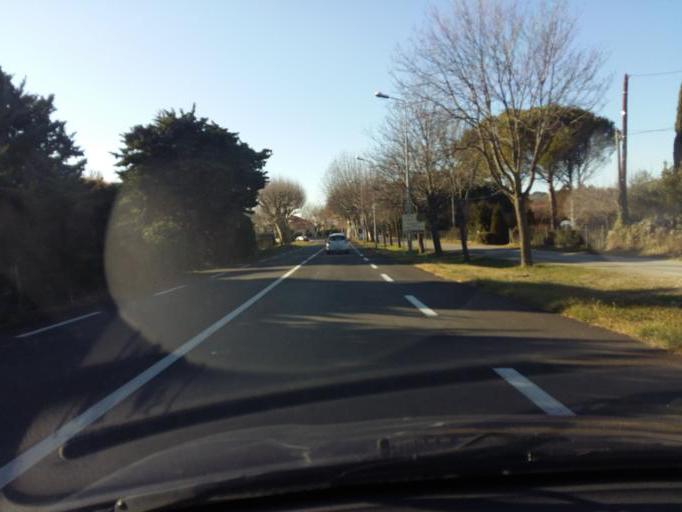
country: FR
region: Provence-Alpes-Cote d'Azur
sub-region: Departement du Vaucluse
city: Grillon
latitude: 44.3972
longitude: 4.9299
